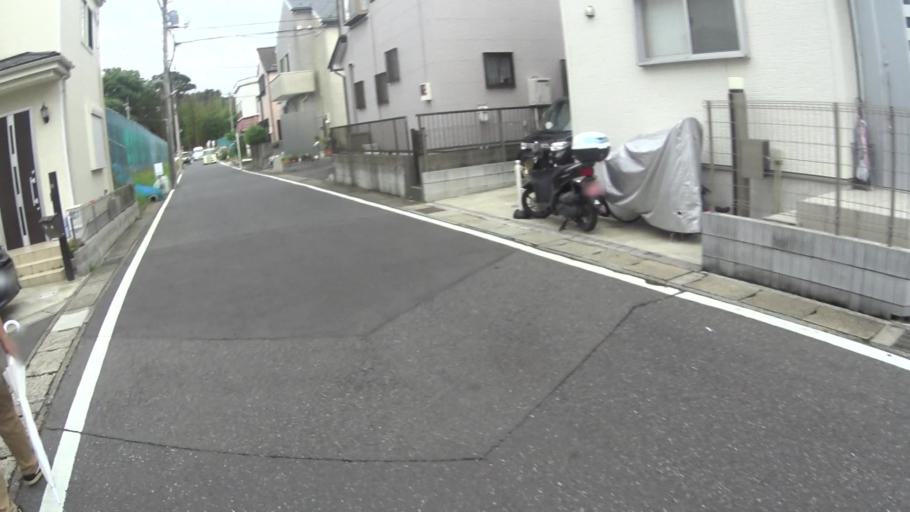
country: JP
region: Chiba
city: Nagareyama
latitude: 35.8359
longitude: 139.9192
